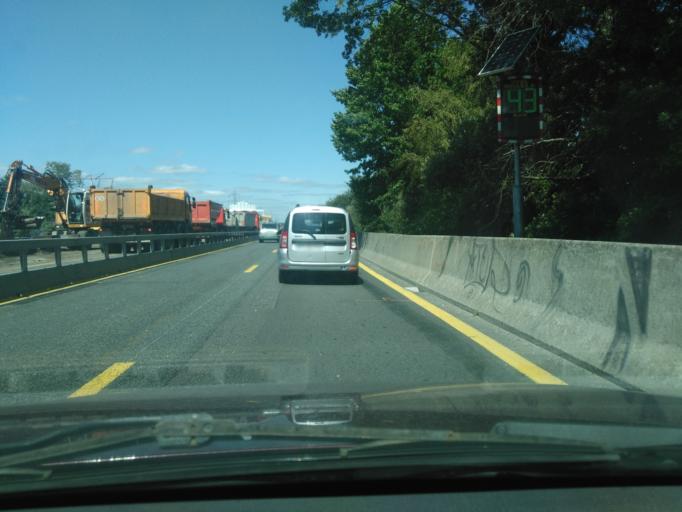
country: FR
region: Aquitaine
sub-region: Departement de la Gironde
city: Pessac
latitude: 44.8241
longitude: -0.6745
